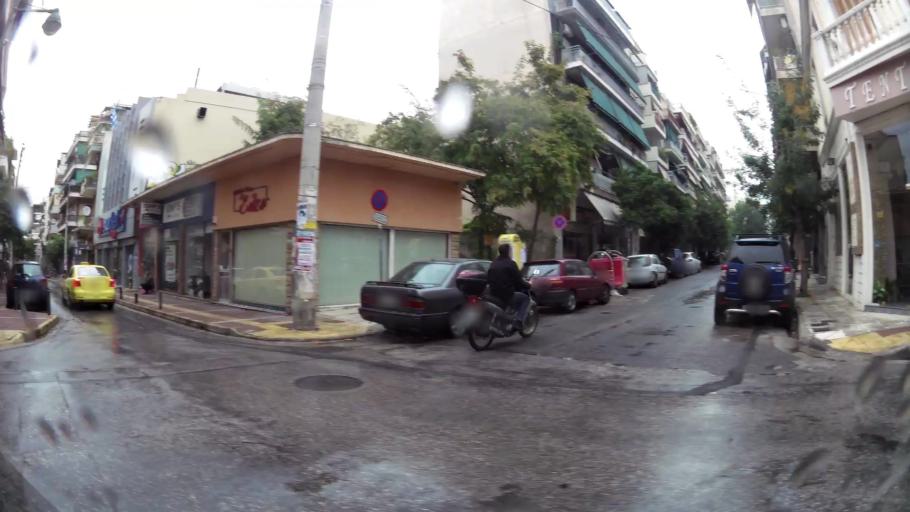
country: GR
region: Attica
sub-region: Nomarchia Athinas
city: Vyronas
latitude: 37.9581
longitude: 23.7535
